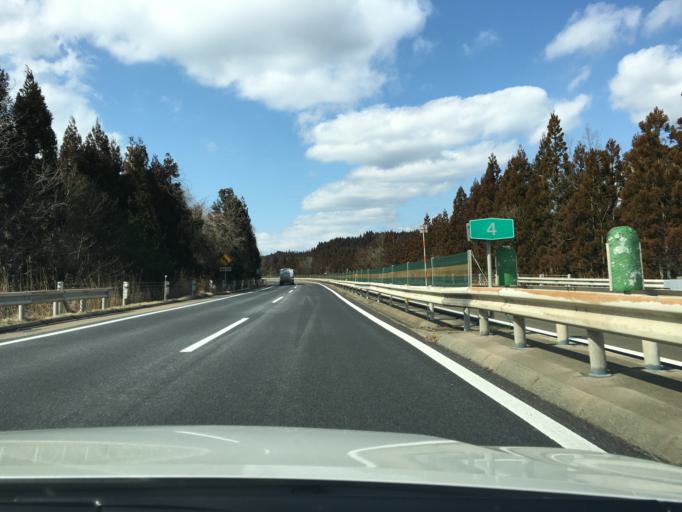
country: JP
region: Miyagi
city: Okawara
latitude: 38.1572
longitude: 140.6873
